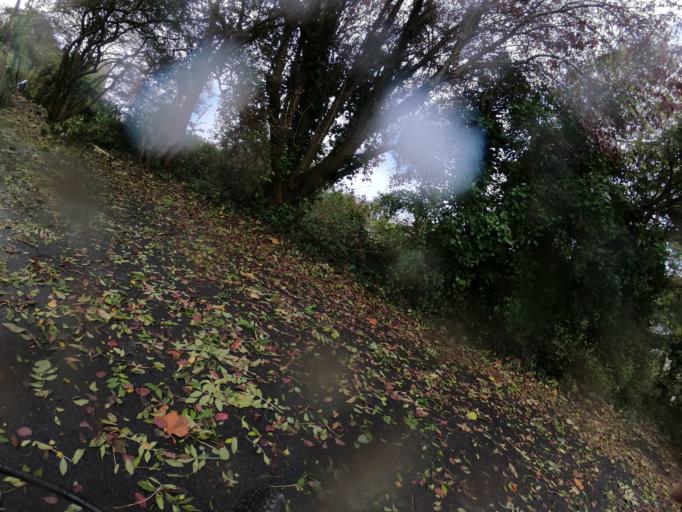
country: GB
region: England
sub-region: Borough of Torbay
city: Brixham
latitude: 50.3856
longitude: -3.5171
